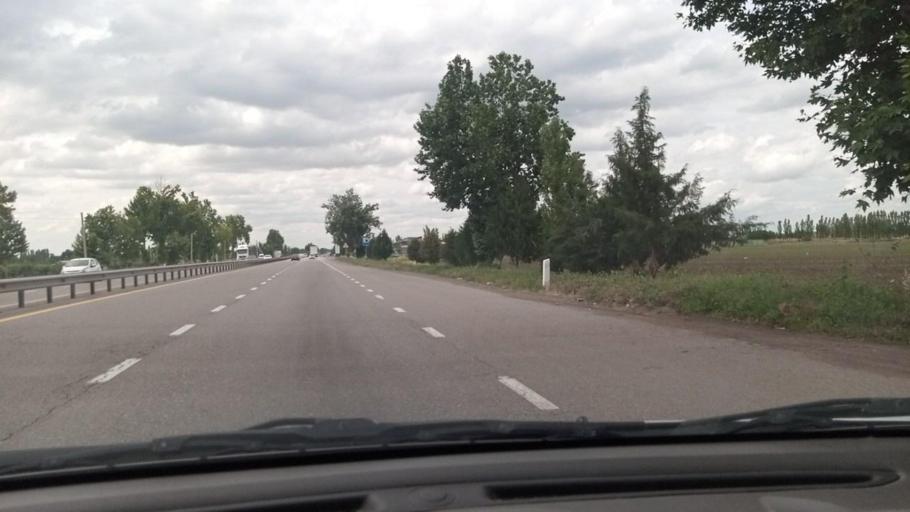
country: UZ
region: Toshkent Shahri
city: Bektemir
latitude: 41.1456
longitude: 69.4310
